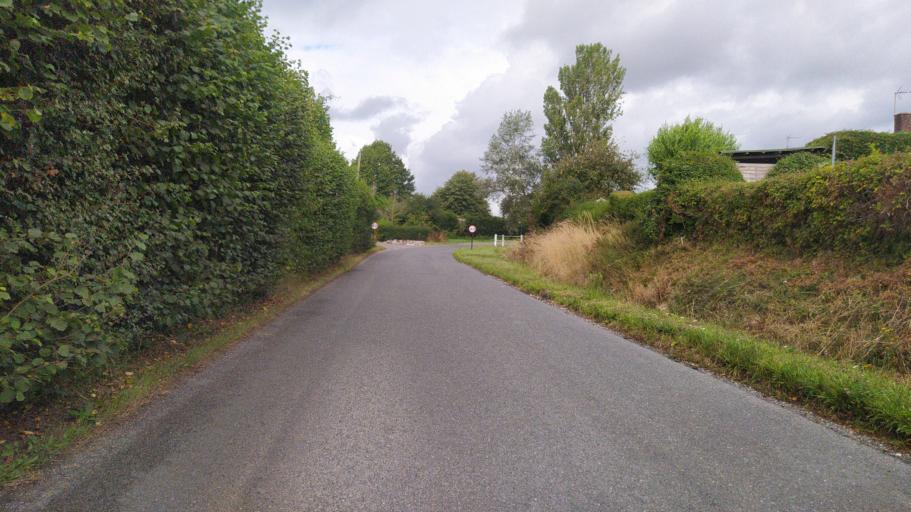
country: GB
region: England
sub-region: Hampshire
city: Petersfield
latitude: 50.9780
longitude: -0.9517
